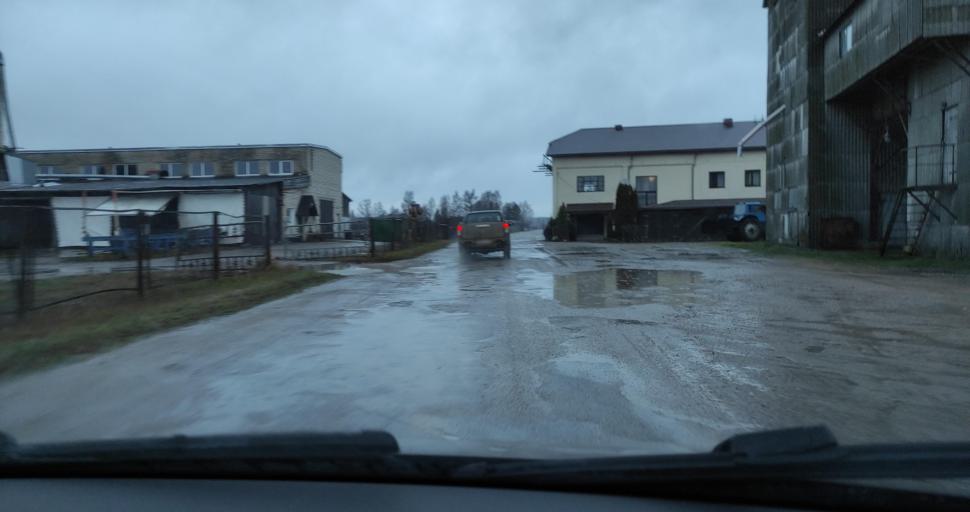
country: LV
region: Skrunda
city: Skrunda
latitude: 56.6706
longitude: 22.2197
